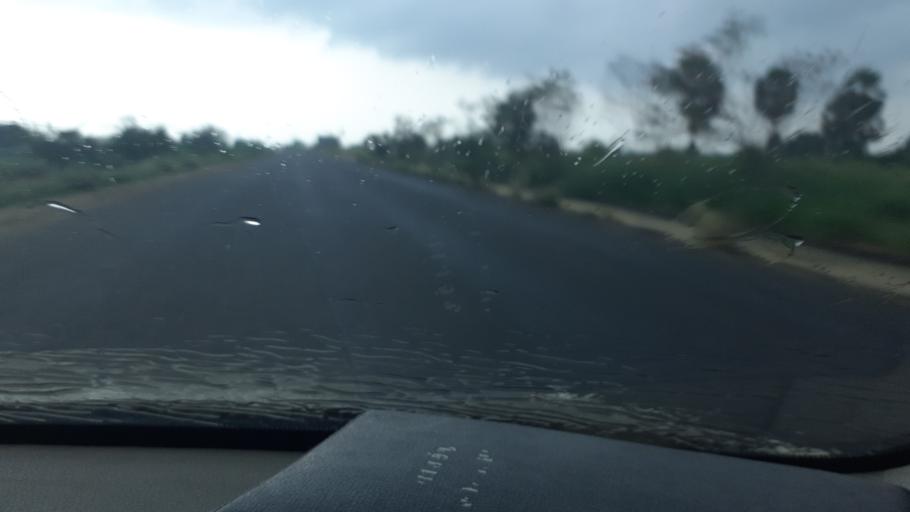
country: IN
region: Tamil Nadu
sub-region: Thoothukkudi
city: Kadambur
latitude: 9.0823
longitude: 77.8019
